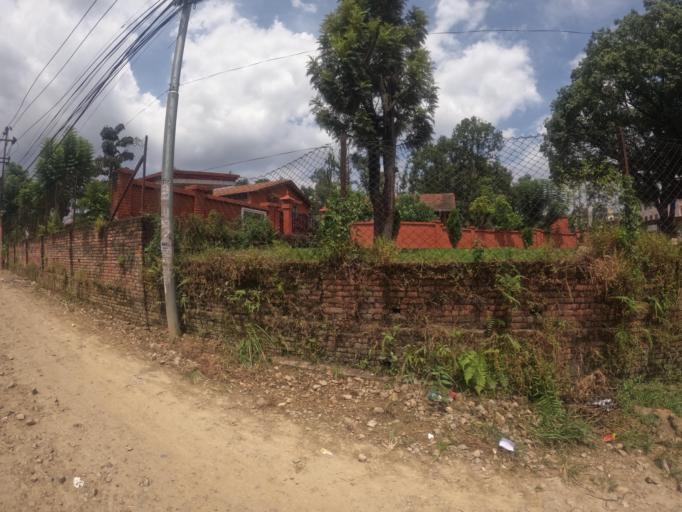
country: NP
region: Central Region
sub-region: Bagmati Zone
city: Bhaktapur
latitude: 27.6802
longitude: 85.3761
